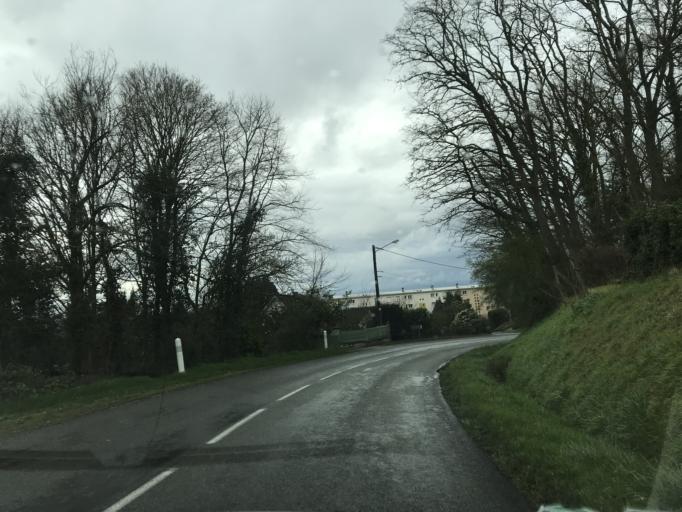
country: FR
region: Picardie
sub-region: Departement de l'Aisne
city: Belleu
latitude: 49.3591
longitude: 3.3432
